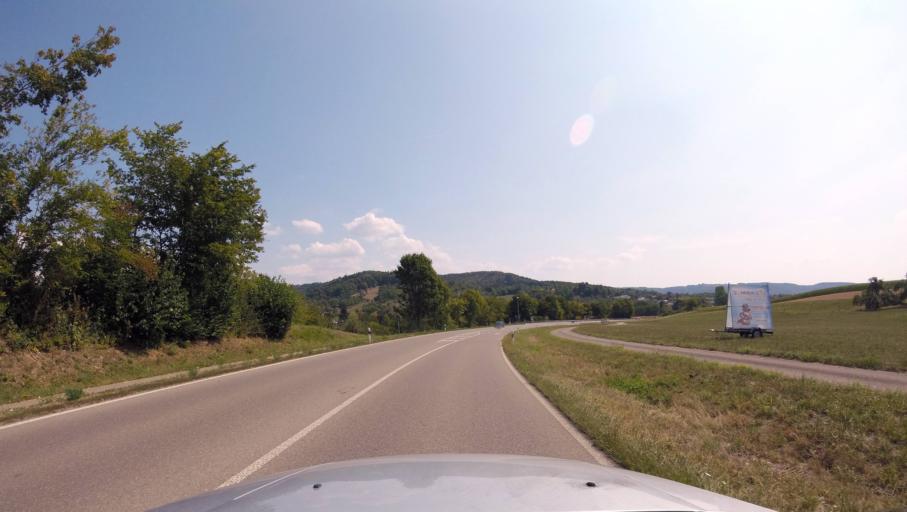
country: DE
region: Baden-Wuerttemberg
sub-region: Regierungsbezirk Stuttgart
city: Oppenweiler
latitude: 48.9538
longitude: 9.4975
